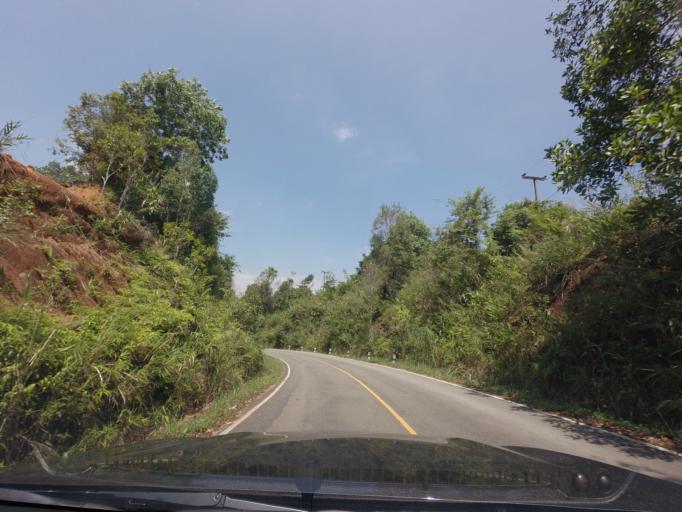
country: TH
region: Loei
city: Na Haeo
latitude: 17.5842
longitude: 100.9073
